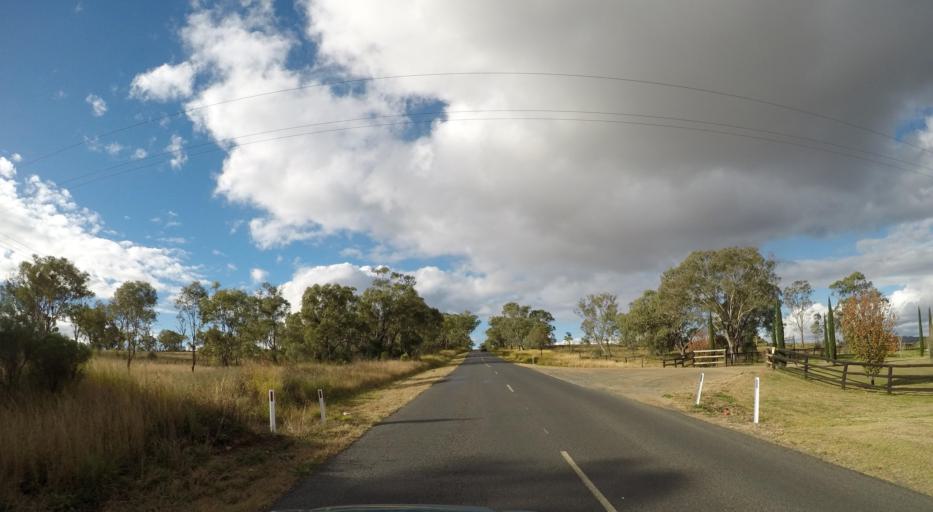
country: AU
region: Queensland
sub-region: Toowoomba
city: Westbrook
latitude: -27.7005
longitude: 151.6620
